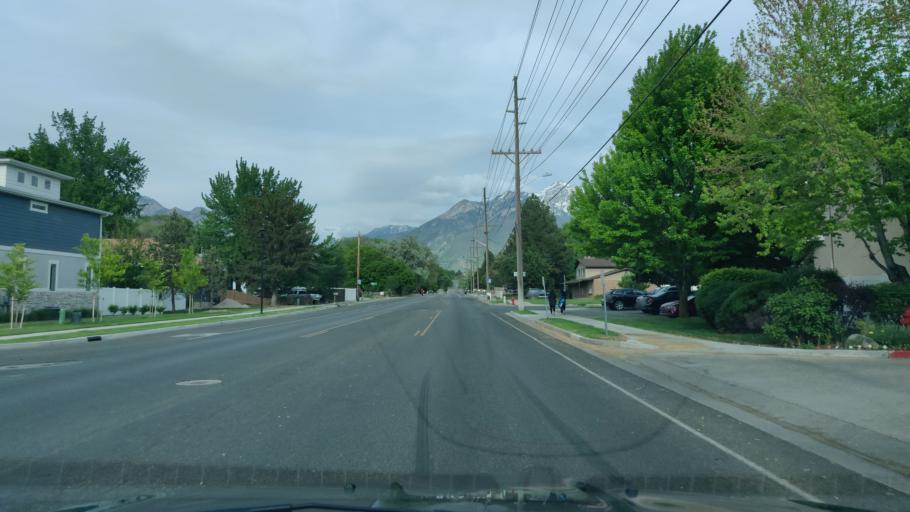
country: US
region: Utah
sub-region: Salt Lake County
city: Sandy City
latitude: 40.6095
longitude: -111.8691
